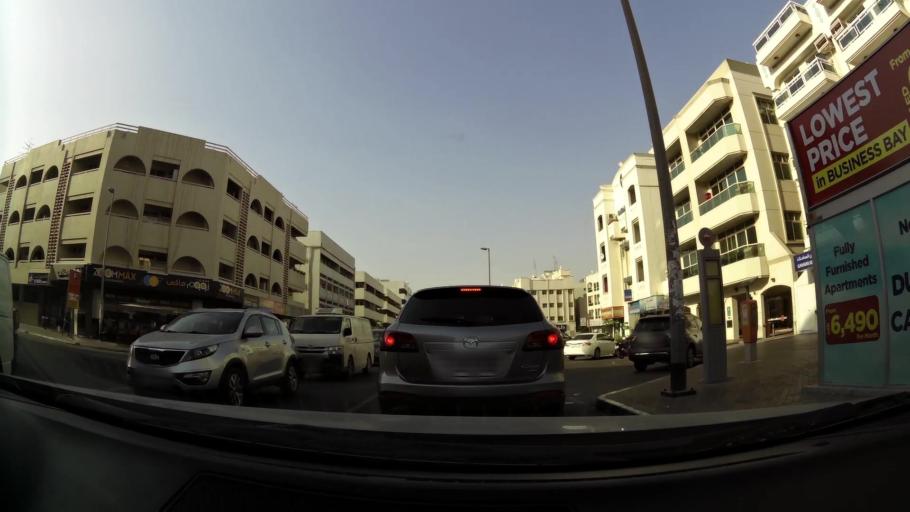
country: AE
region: Ash Shariqah
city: Sharjah
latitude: 25.2466
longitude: 55.3022
